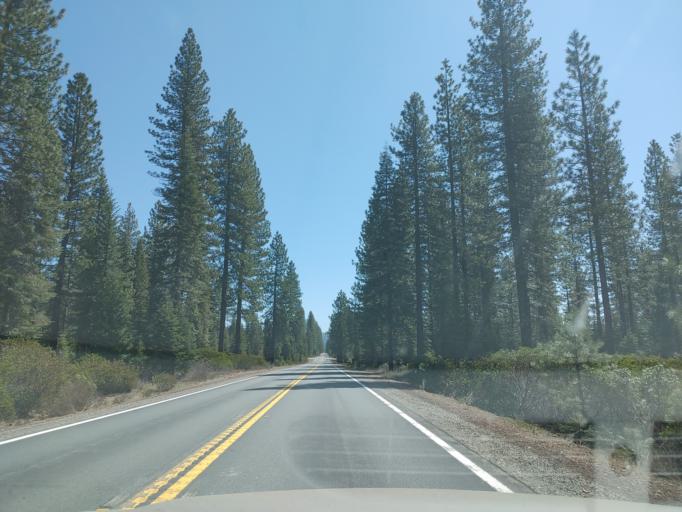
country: US
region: California
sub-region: Siskiyou County
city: McCloud
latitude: 41.2610
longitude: -121.8439
